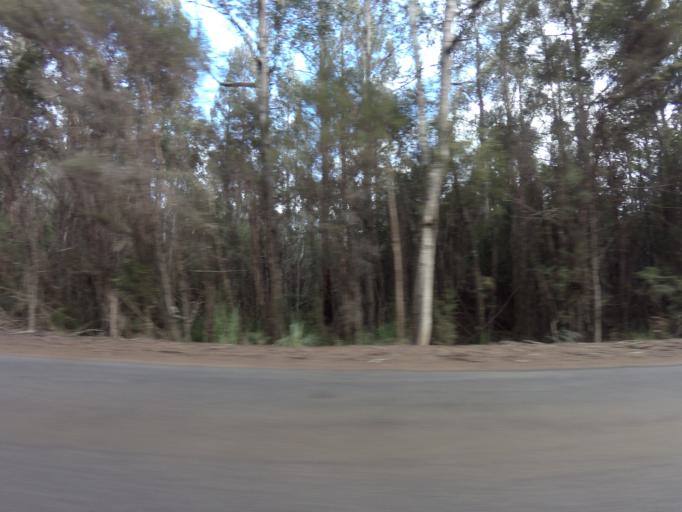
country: AU
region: Tasmania
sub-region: Huon Valley
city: Geeveston
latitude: -43.3919
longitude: 146.9575
